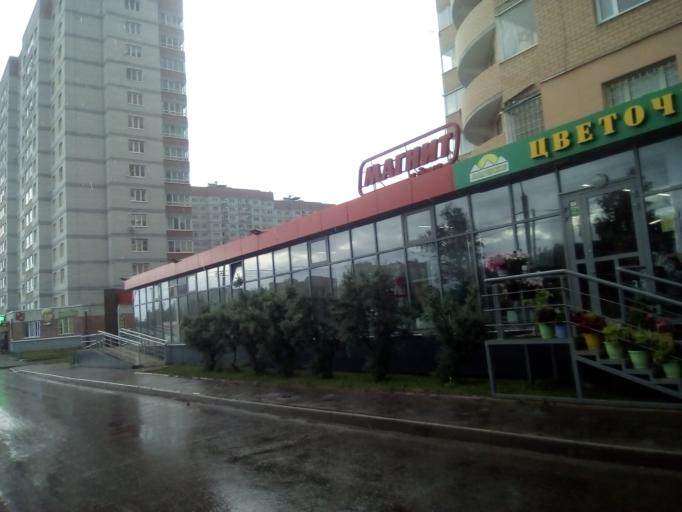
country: RU
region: Jaroslavl
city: Yaroslavl
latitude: 57.5856
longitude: 39.9072
